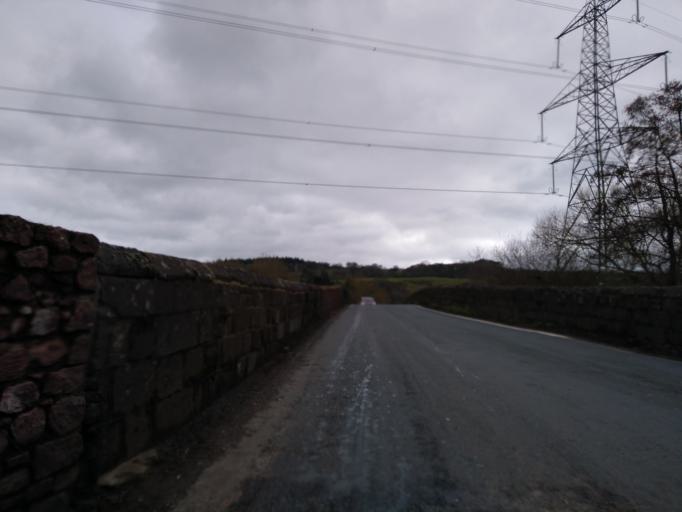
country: GB
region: England
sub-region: Devon
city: Exeter
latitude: 50.7682
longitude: -3.5075
